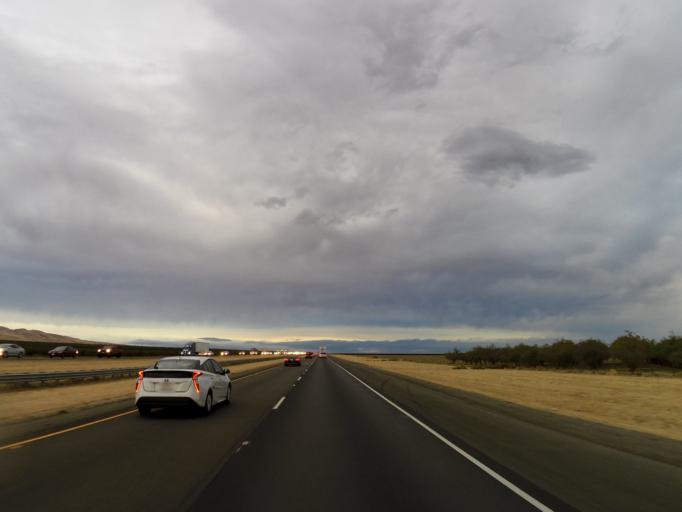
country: US
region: California
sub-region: Fresno County
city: Firebaugh
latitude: 36.6976
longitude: -120.6670
